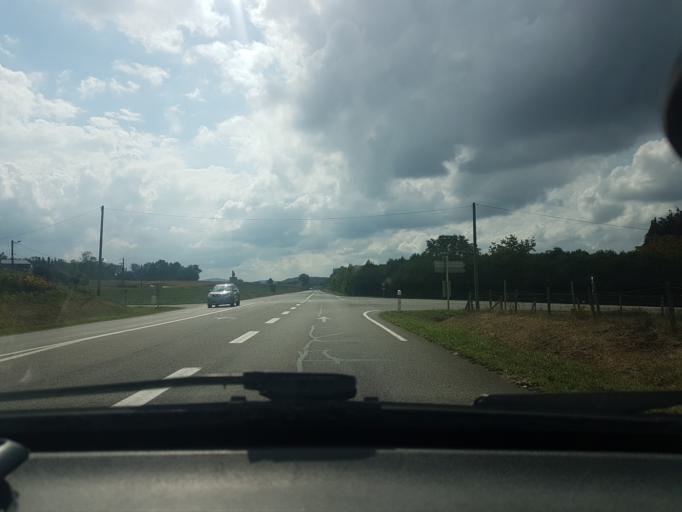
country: FR
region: Franche-Comte
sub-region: Departement de la Haute-Saone
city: Villersexel
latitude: 47.5435
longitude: 6.4313
